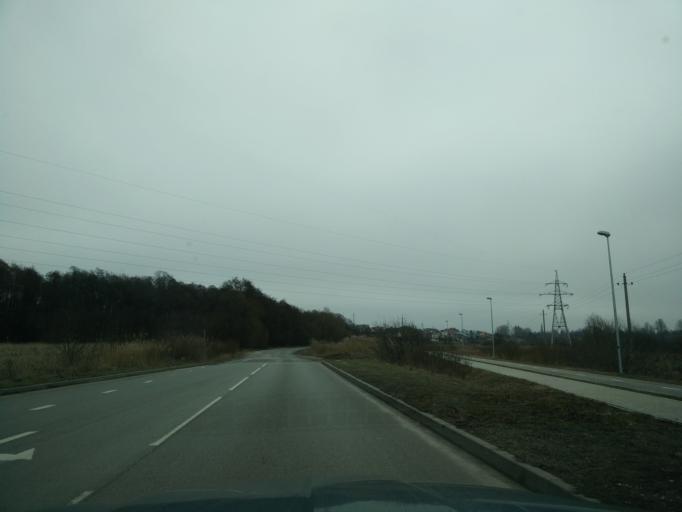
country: LT
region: Klaipedos apskritis
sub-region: Klaipeda
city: Klaipeda
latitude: 55.7258
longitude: 21.1669
